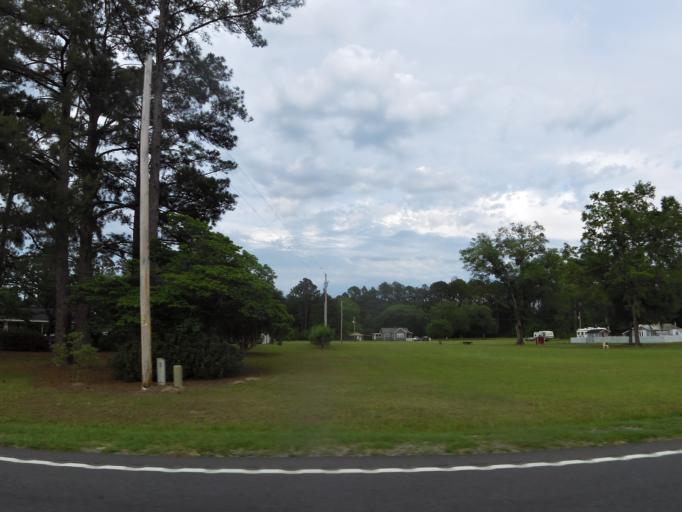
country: US
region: South Carolina
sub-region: Jasper County
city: Hardeeville
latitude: 32.3194
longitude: -81.0890
